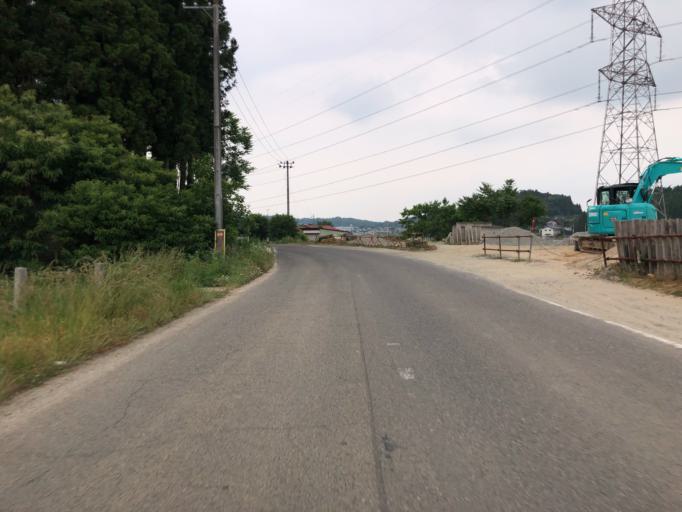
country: JP
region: Fukushima
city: Nihommatsu
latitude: 37.6458
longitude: 140.4735
